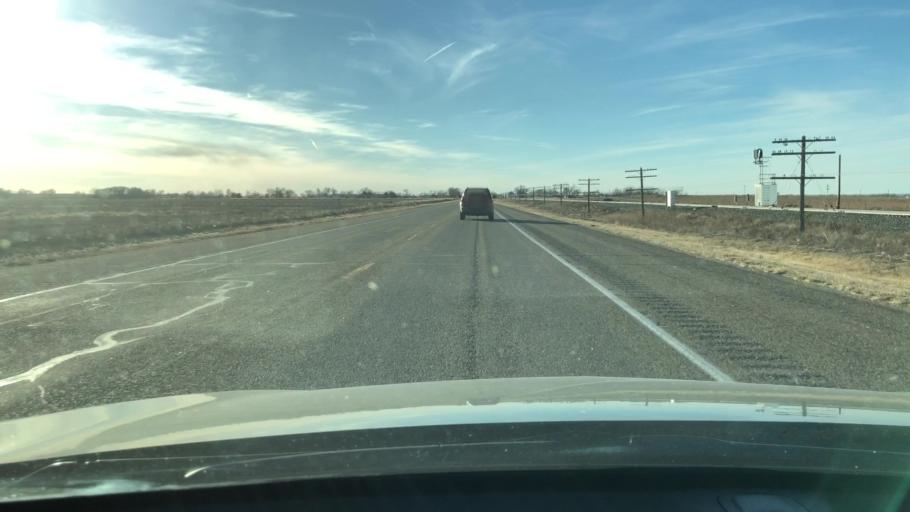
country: US
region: Colorado
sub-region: Prowers County
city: Lamar
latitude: 38.0827
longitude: -102.4001
